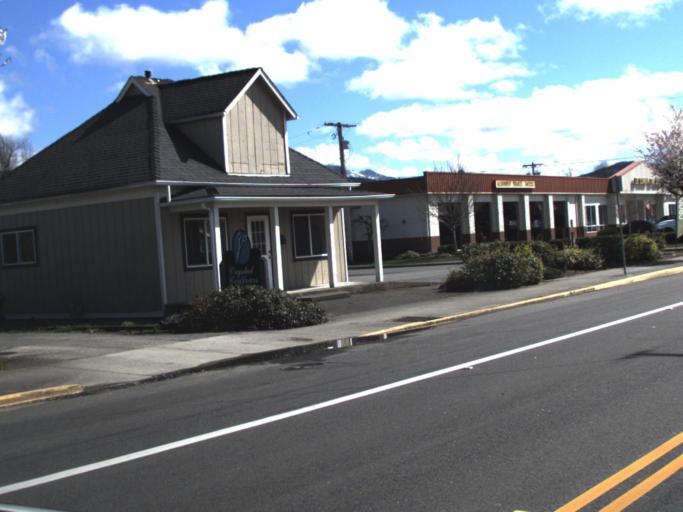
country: US
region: Washington
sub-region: King County
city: Enumclaw
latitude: 47.2016
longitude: -121.9857
